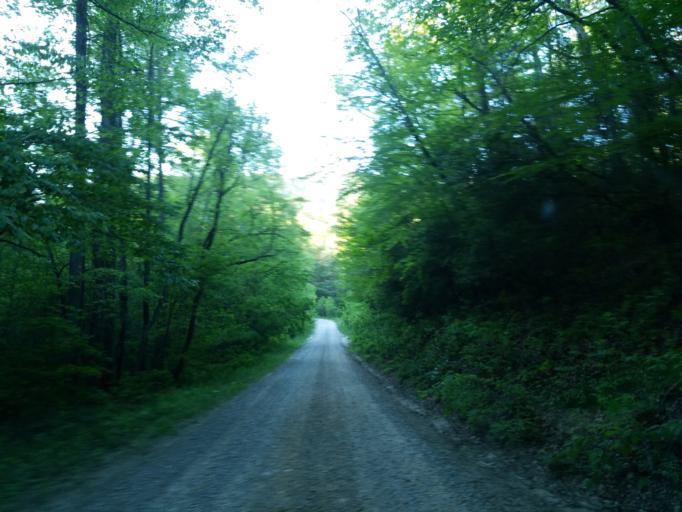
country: US
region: Georgia
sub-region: Lumpkin County
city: Dahlonega
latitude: 34.6783
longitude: -84.1328
